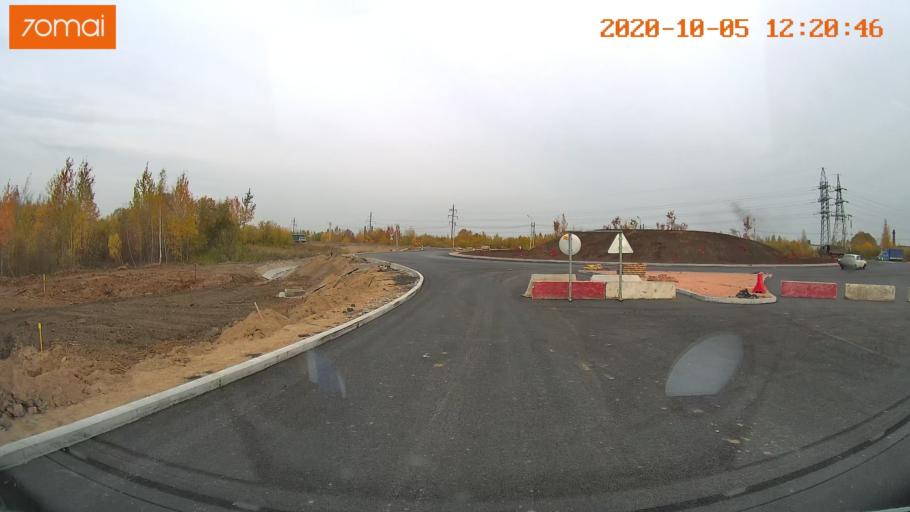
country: RU
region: Ivanovo
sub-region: Gorod Ivanovo
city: Ivanovo
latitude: 56.9662
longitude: 40.9318
